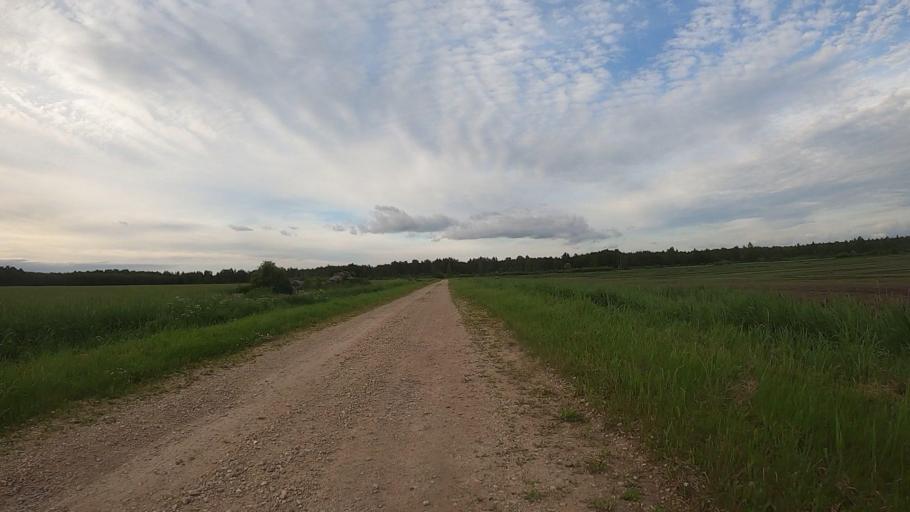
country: LV
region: Olaine
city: Olaine
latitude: 56.8261
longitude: 23.9583
